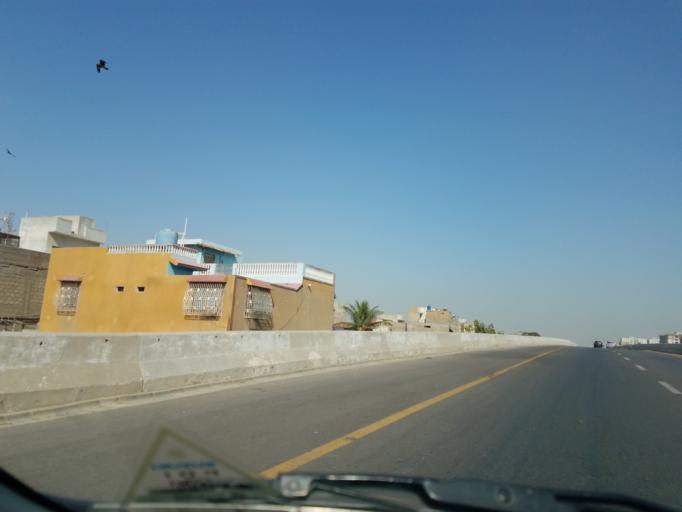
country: PK
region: Sindh
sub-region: Karachi District
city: Karachi
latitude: 24.8905
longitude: 67.0297
